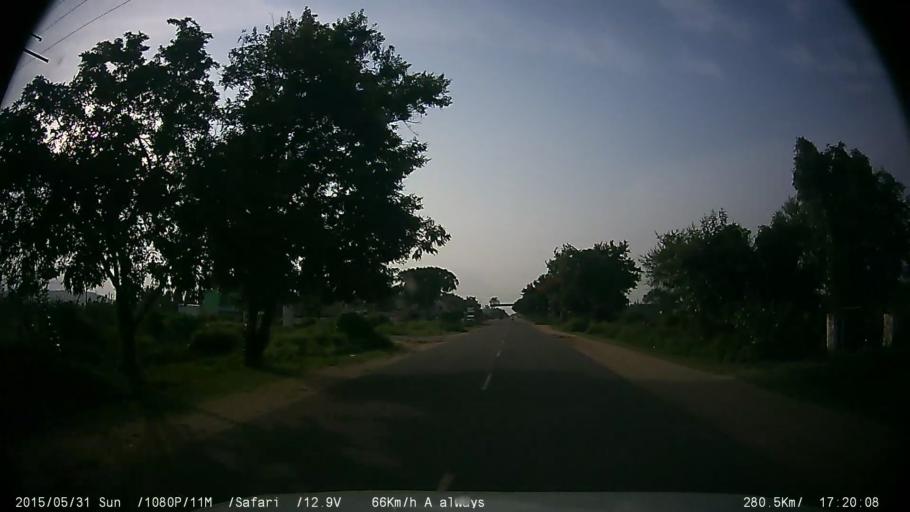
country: IN
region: Karnataka
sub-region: Chamrajnagar
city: Gundlupet
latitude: 11.8206
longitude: 76.6825
